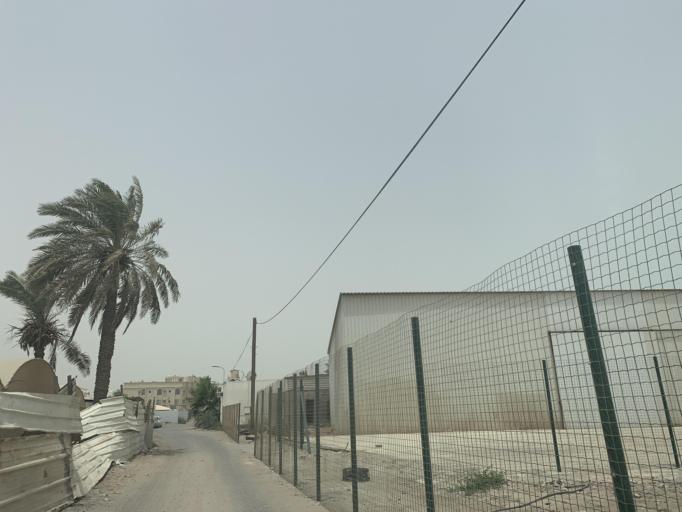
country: BH
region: Manama
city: Jidd Hafs
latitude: 26.2309
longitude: 50.5171
